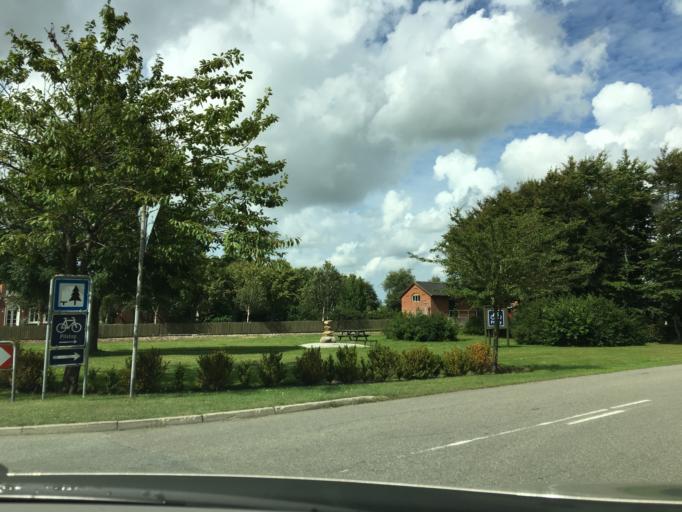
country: DK
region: South Denmark
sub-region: Varde Kommune
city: Oksbol
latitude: 55.7096
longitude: 8.3039
